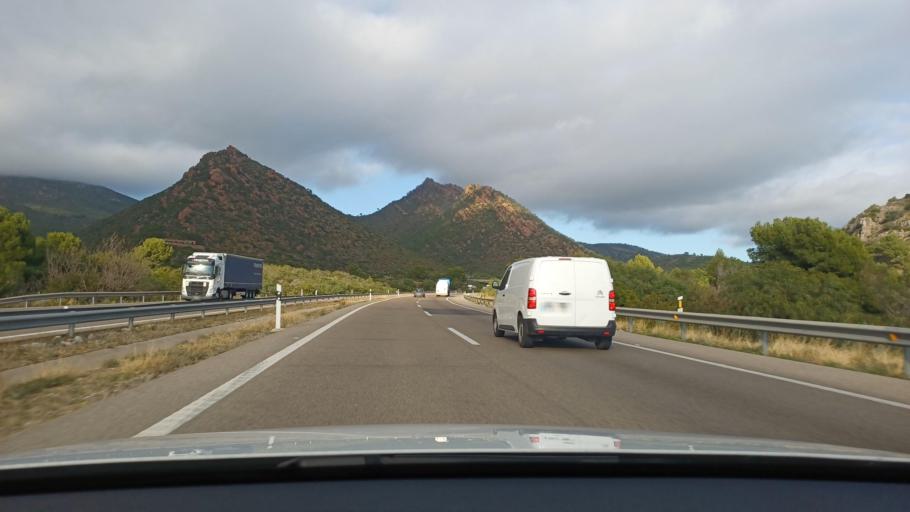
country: ES
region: Valencia
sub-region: Provincia de Castello
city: Benicassim
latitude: 40.0563
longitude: 0.0426
